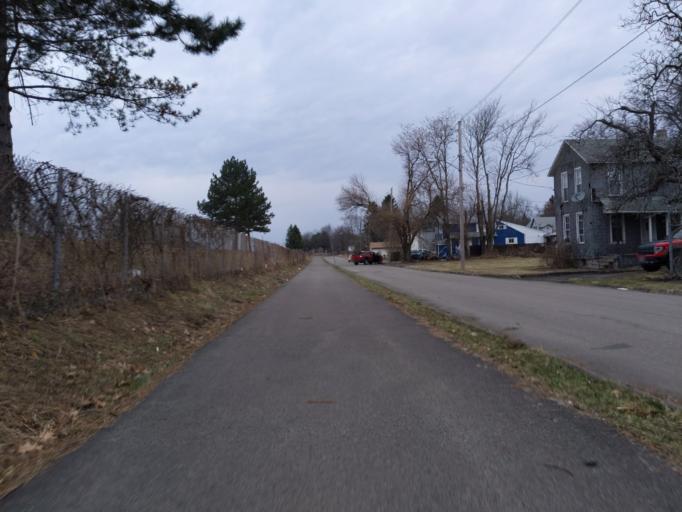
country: US
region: New York
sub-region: Chemung County
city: Elmira
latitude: 42.1082
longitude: -76.8121
